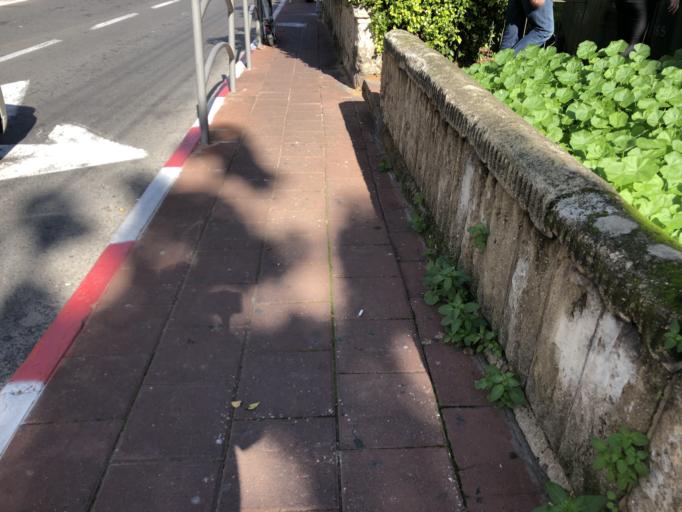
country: IL
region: Tel Aviv
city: Bene Beraq
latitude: 32.0743
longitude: 34.8250
